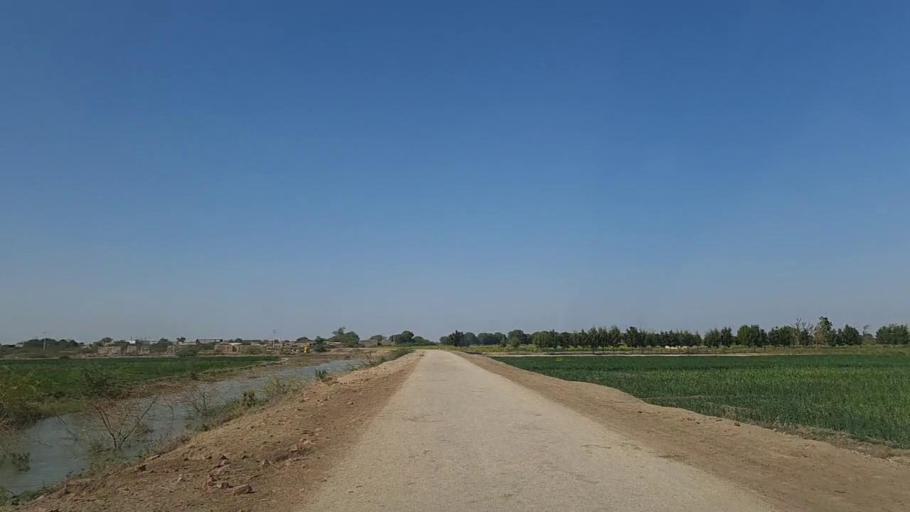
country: PK
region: Sindh
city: Naukot
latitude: 25.0014
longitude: 69.3381
